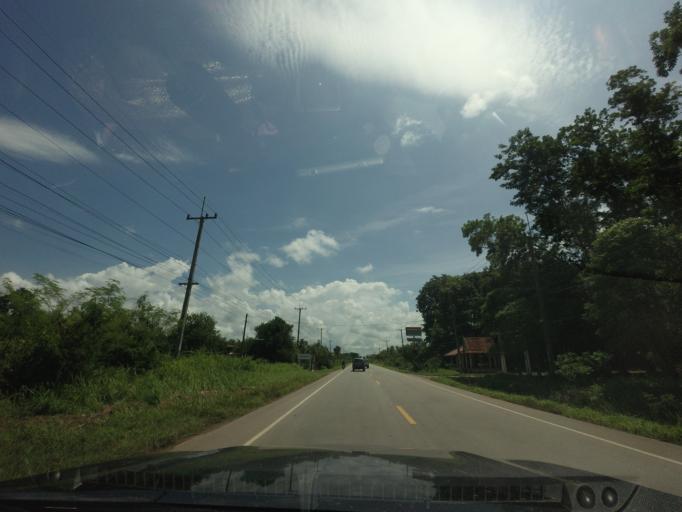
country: TH
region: Changwat Udon Thani
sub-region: Amphoe Ban Phue
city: Ban Phue
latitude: 17.7016
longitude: 102.4396
